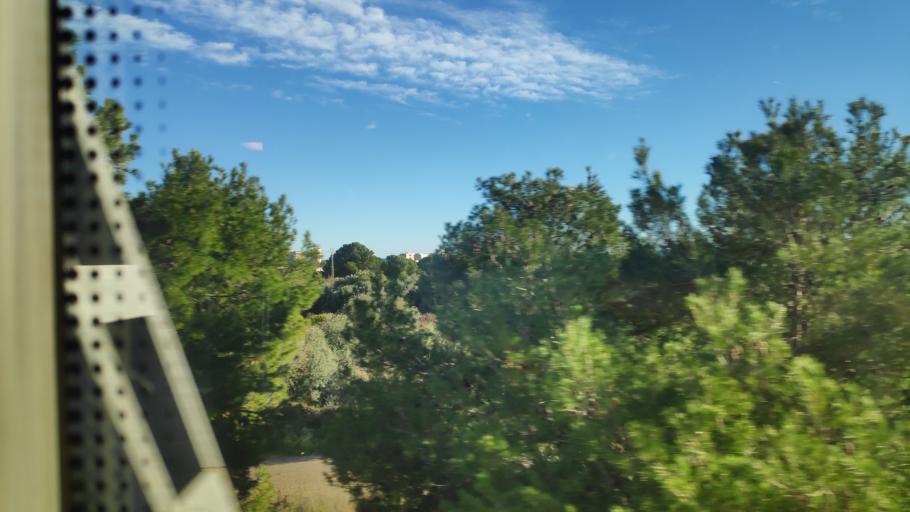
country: ES
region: Valencia
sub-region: Provincia de Castello
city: Benicassim
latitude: 40.0457
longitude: 0.0401
